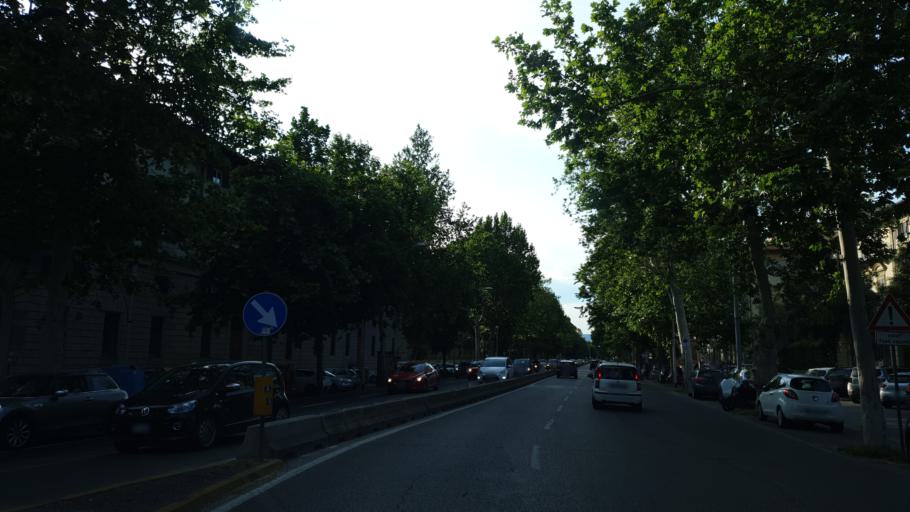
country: IT
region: Tuscany
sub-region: Province of Florence
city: Florence
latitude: 43.7783
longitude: 11.2673
